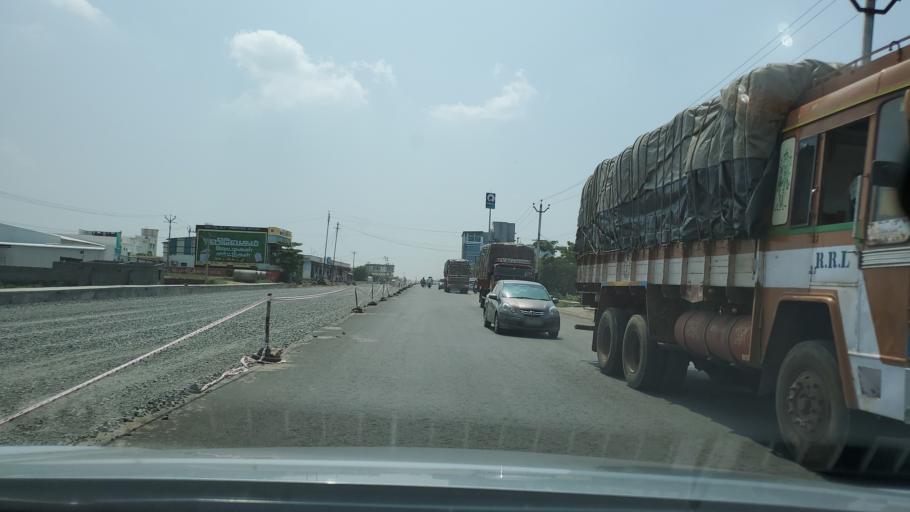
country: IN
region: Tamil Nadu
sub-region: Tiruppur
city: Dharapuram
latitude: 10.7420
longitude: 77.5186
